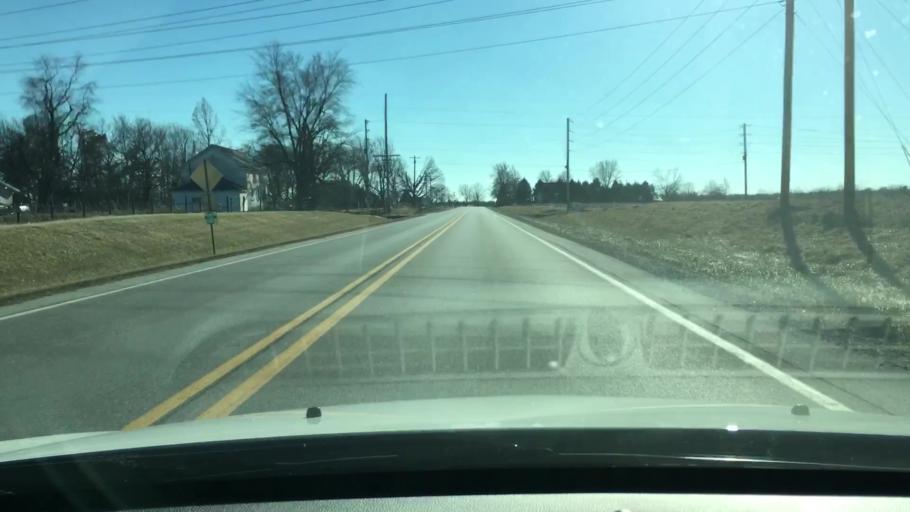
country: US
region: Illinois
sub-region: Pike County
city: Pittsfield
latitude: 39.6505
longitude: -90.7842
